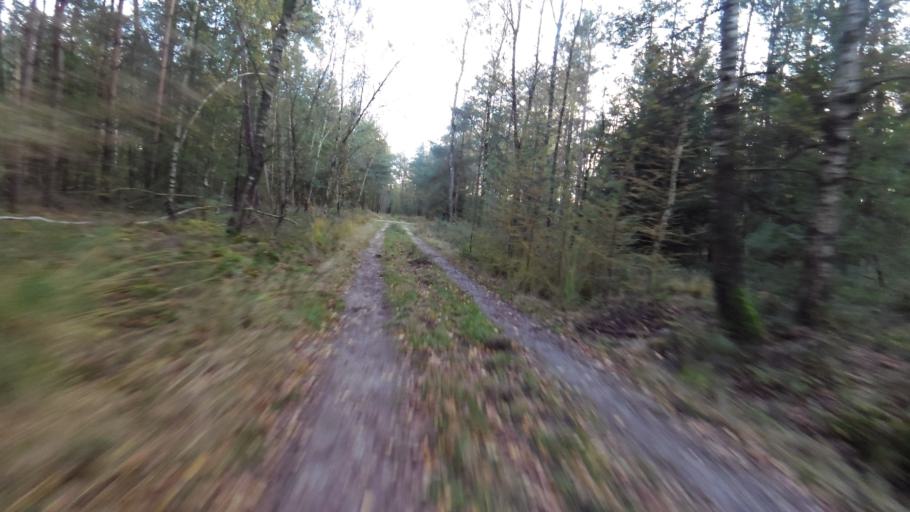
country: NL
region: Gelderland
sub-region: Gemeente Epe
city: Emst
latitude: 52.3490
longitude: 5.8985
